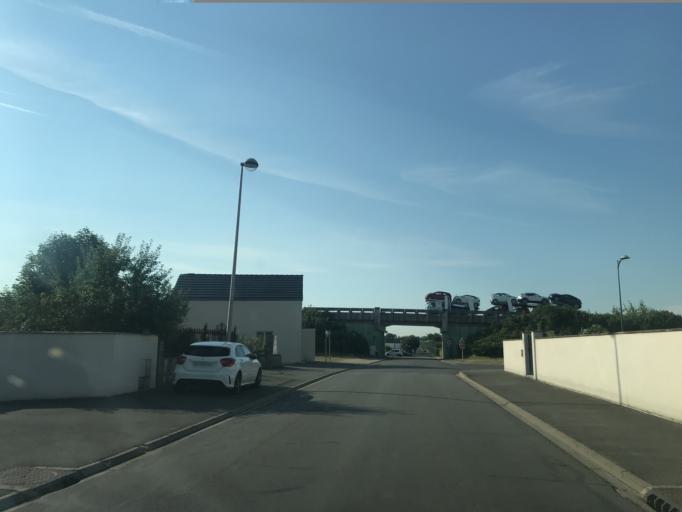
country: FR
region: Centre
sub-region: Departement du Loiret
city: Ormes
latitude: 47.9459
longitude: 1.8192
